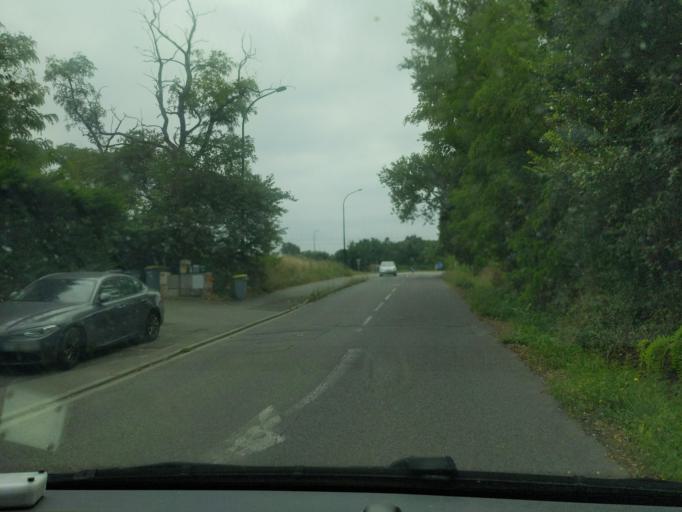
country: FR
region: Midi-Pyrenees
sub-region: Departement de la Haute-Garonne
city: Auzeville-Tolosane
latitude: 43.5340
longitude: 1.4773
